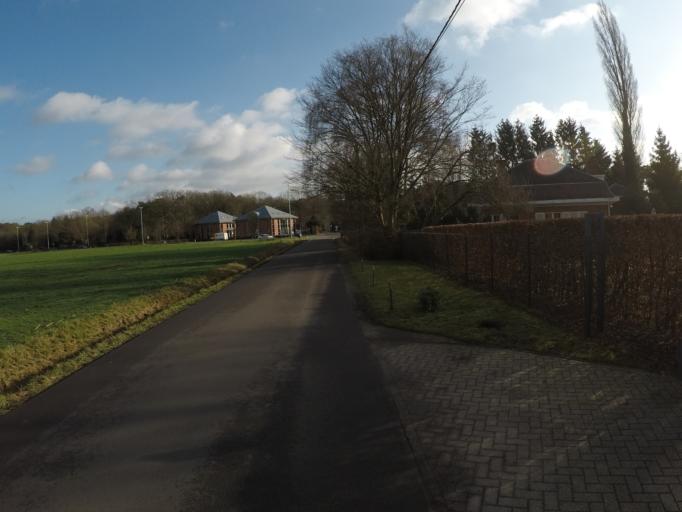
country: BE
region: Flanders
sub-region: Provincie Antwerpen
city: Zandhoven
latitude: 51.2365
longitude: 4.6897
